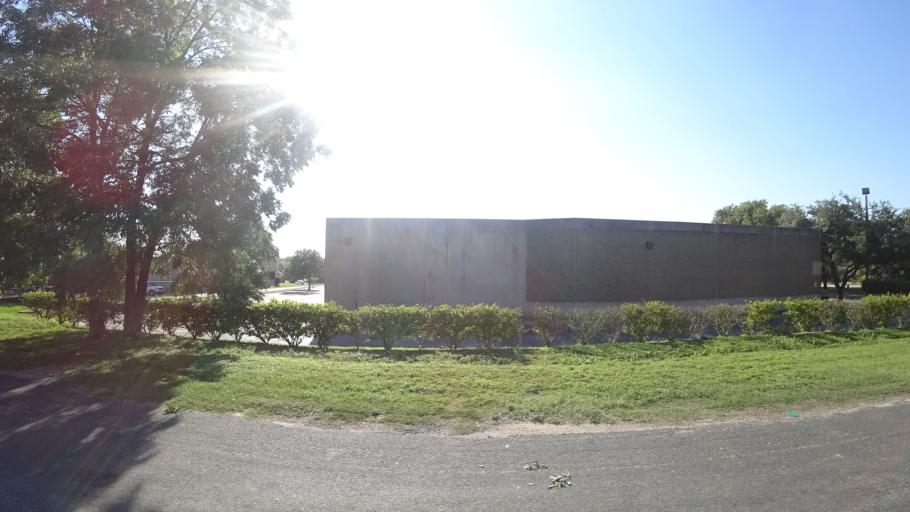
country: US
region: Texas
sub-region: Travis County
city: Austin
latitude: 30.3433
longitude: -97.6762
